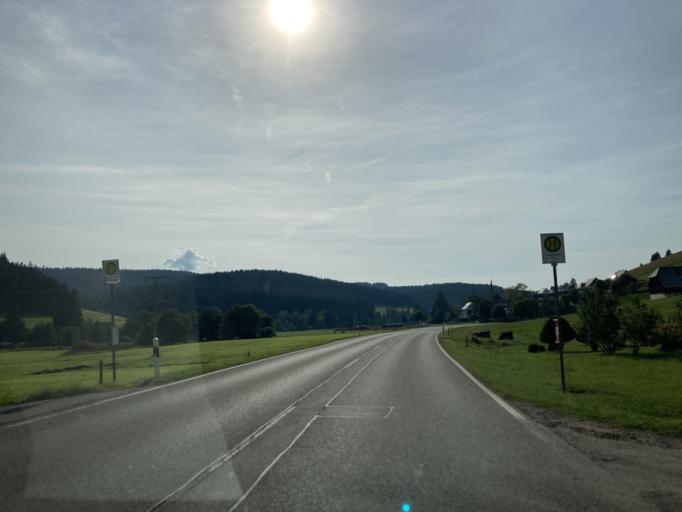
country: DE
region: Baden-Wuerttemberg
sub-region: Freiburg Region
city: Furtwangen im Schwarzwald
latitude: 48.0474
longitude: 8.2418
